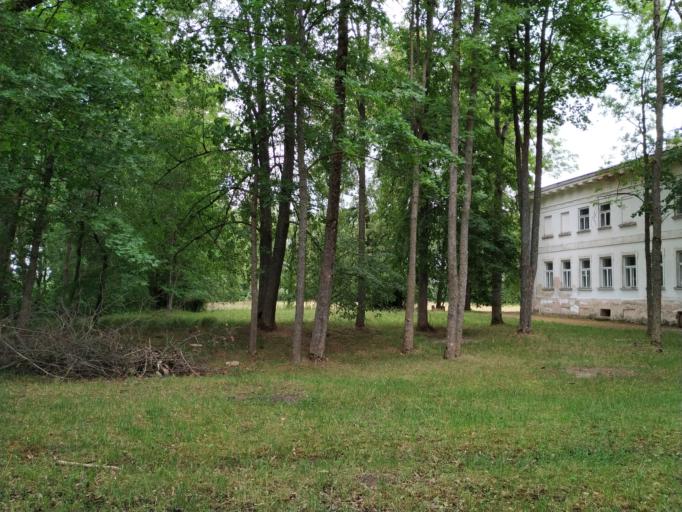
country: LT
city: Vabalninkas
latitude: 55.9083
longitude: 24.8058
